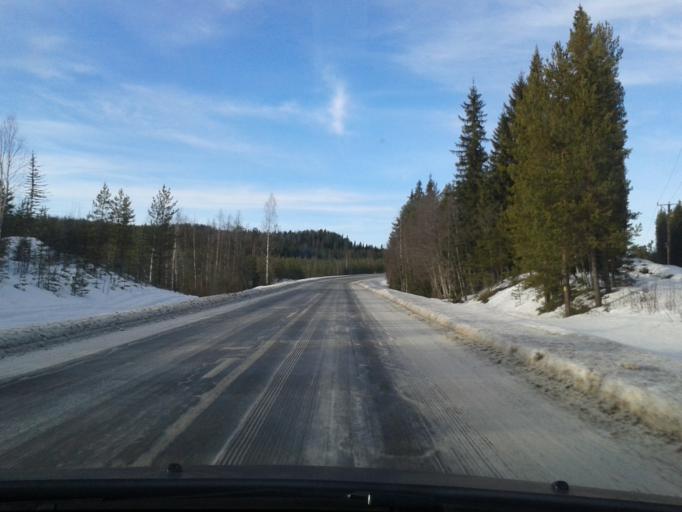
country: SE
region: Vaesternorrland
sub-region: OErnskoeldsviks Kommun
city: Bredbyn
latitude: 63.5529
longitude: 17.9464
